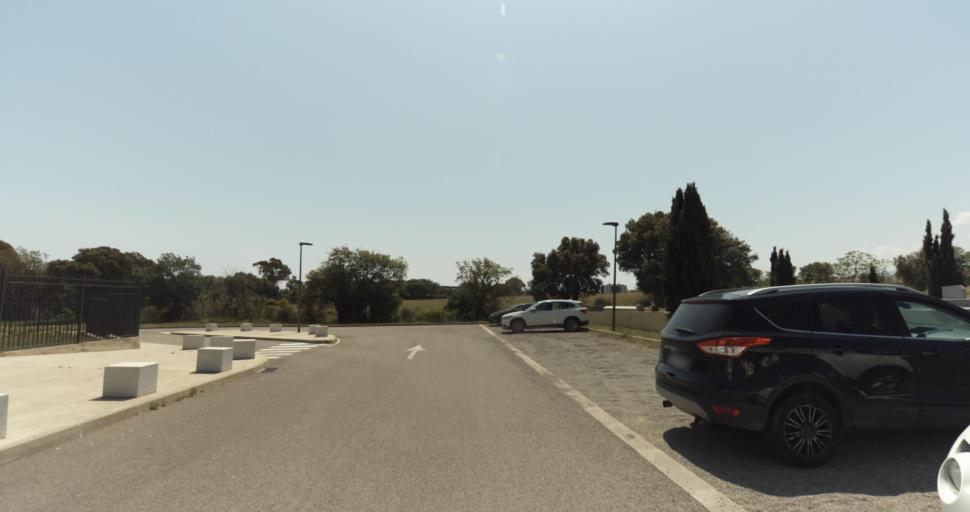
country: FR
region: Corsica
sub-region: Departement de la Haute-Corse
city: Biguglia
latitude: 42.5997
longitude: 9.4335
